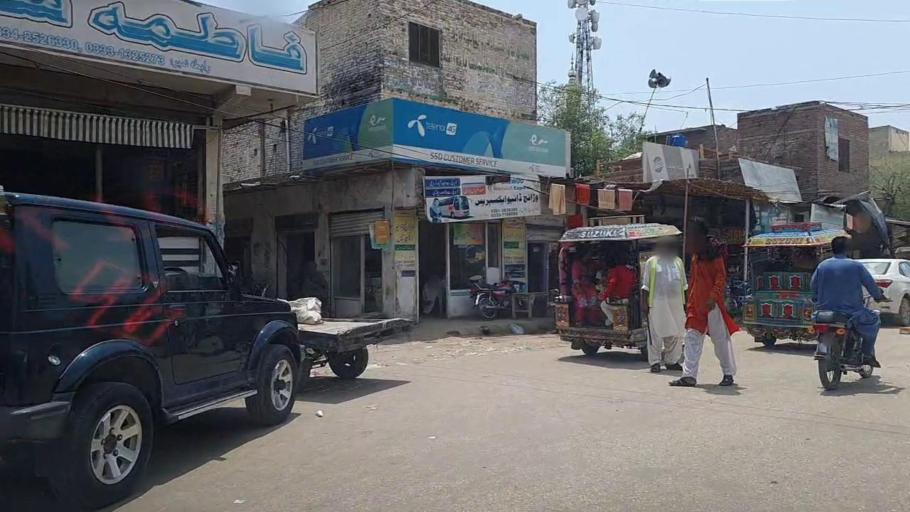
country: PK
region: Sindh
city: Khairpur
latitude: 28.0522
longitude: 69.7002
